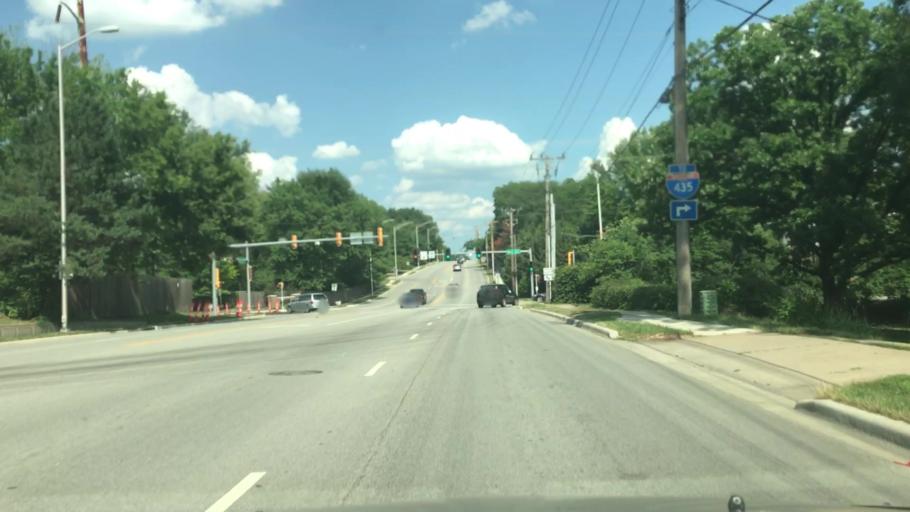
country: US
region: Kansas
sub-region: Johnson County
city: Leawood
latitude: 38.9421
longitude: -94.6405
